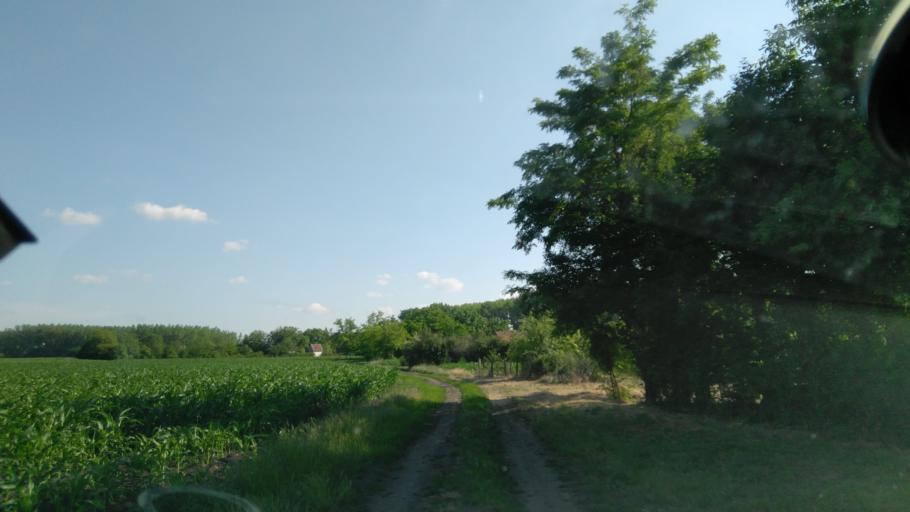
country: HU
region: Bekes
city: Doboz
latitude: 46.7052
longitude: 21.2331
